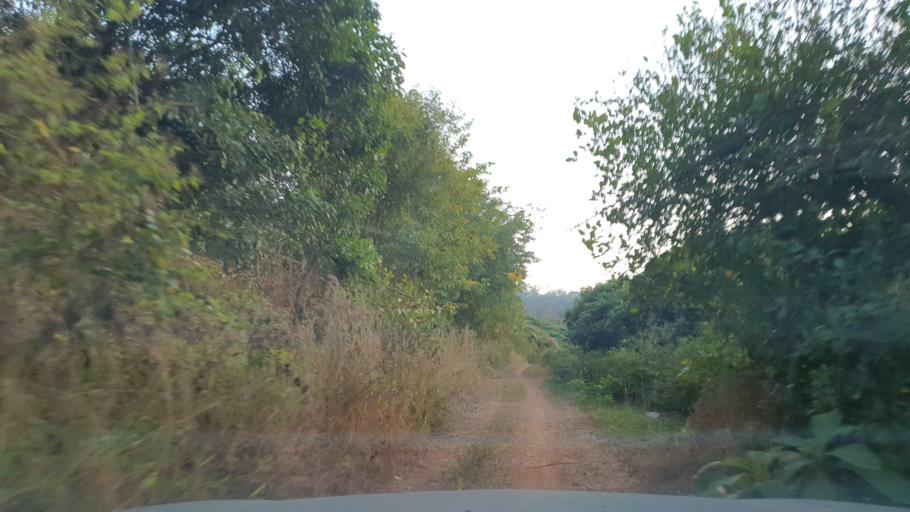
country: TH
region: Chiang Mai
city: Mae Wang
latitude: 18.6952
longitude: 98.8150
